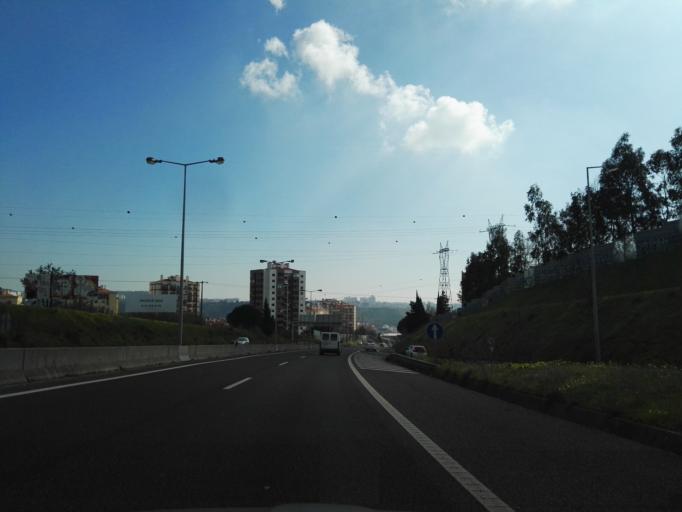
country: PT
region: Lisbon
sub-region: Odivelas
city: Povoa de Santo Adriao
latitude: 38.8008
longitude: -9.1767
